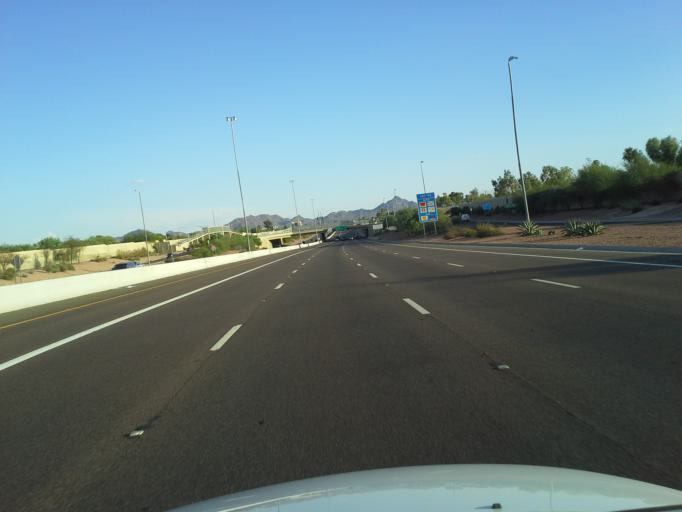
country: US
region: Arizona
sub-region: Maricopa County
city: Paradise Valley
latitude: 33.6587
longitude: -112.0000
